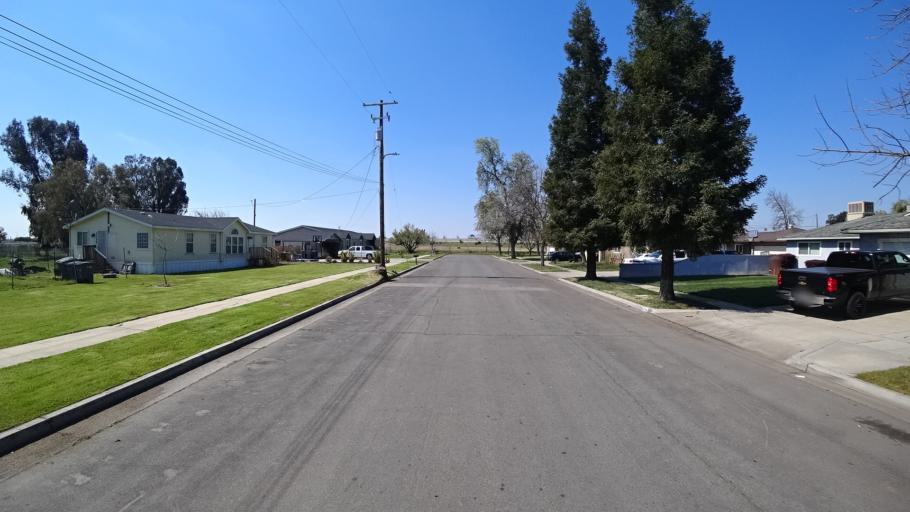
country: US
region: California
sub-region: Fresno County
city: Tarpey Village
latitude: 36.7977
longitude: -119.7398
